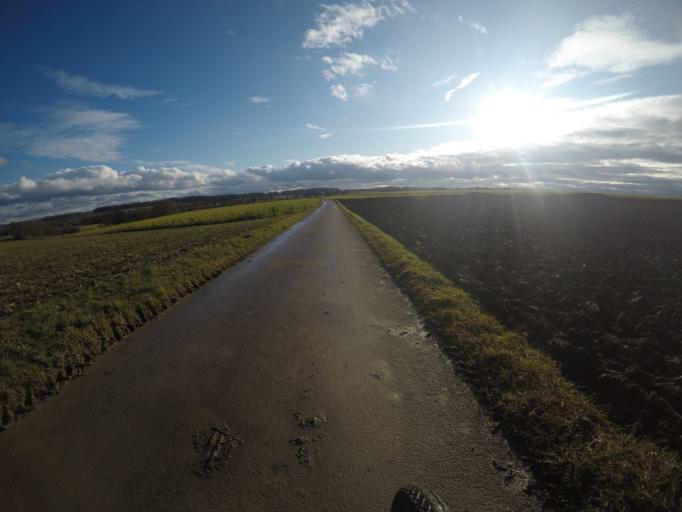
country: DE
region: Baden-Wuerttemberg
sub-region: Regierungsbezirk Stuttgart
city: Bondorf
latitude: 48.5398
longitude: 8.8740
